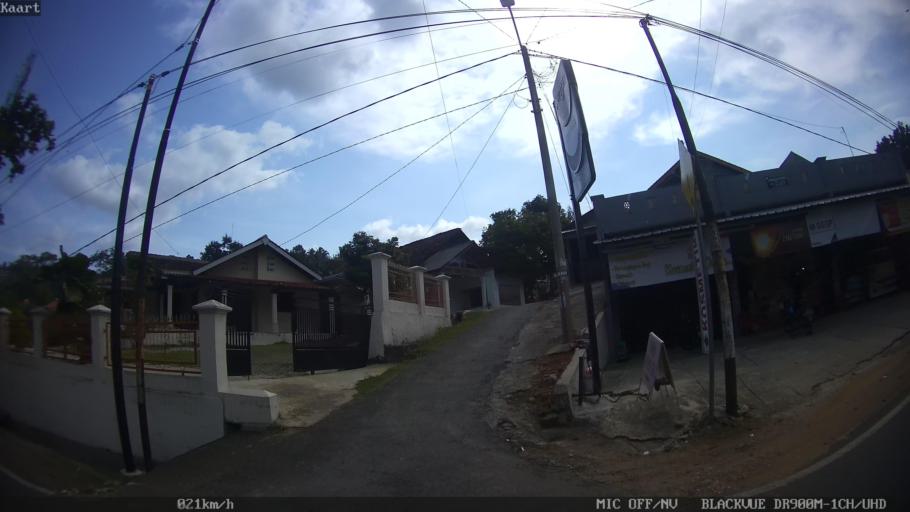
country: ID
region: Lampung
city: Bandarlampung
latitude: -5.4030
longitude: 105.2118
